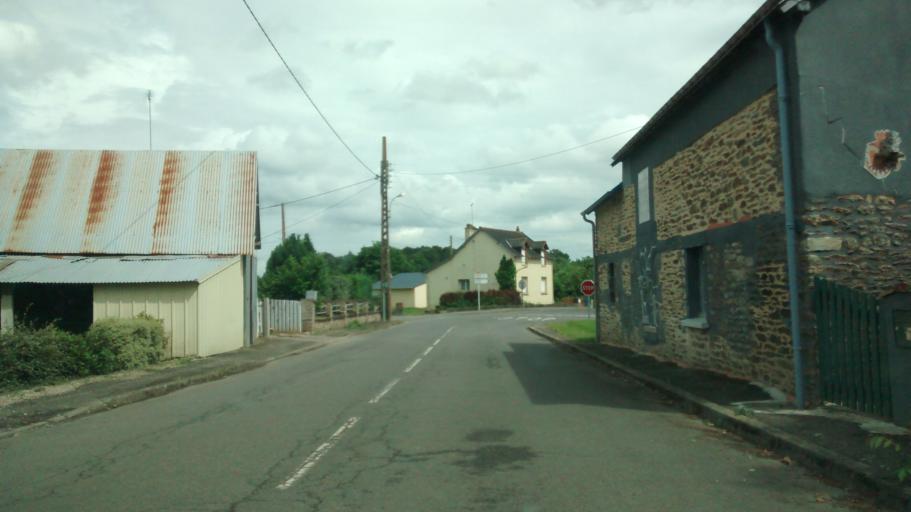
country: FR
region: Brittany
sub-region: Departement du Morbihan
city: Ruffiac
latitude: 47.8362
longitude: -2.2236
